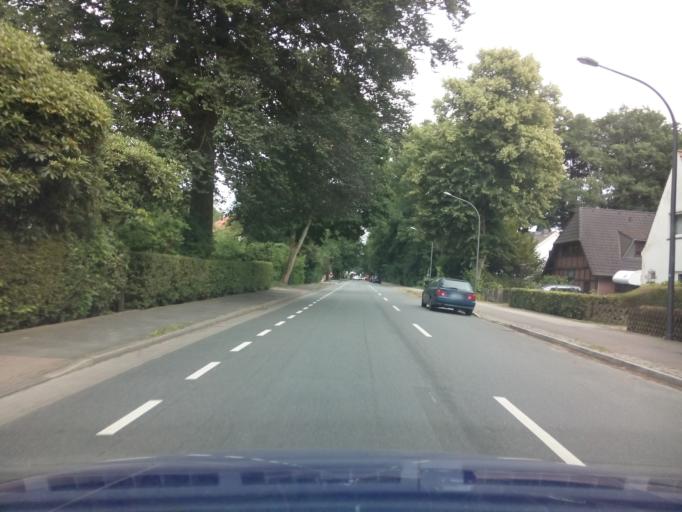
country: DE
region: Lower Saxony
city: Lemwerder
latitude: 53.1745
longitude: 8.6710
